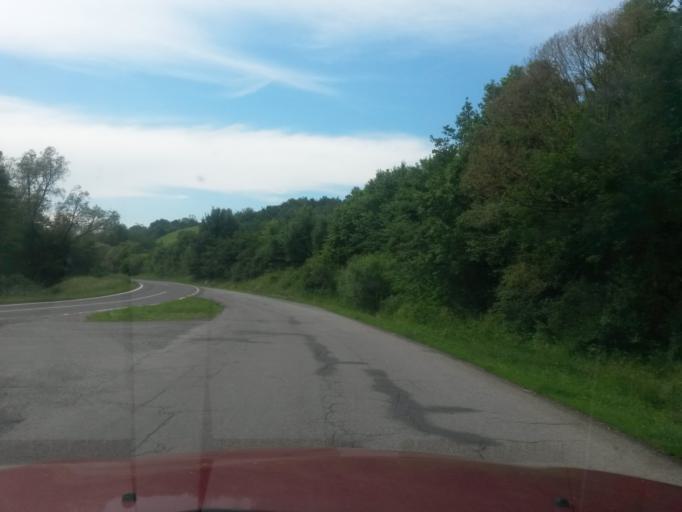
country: SK
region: Presovsky
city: Snina
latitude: 48.9880
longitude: 22.2566
